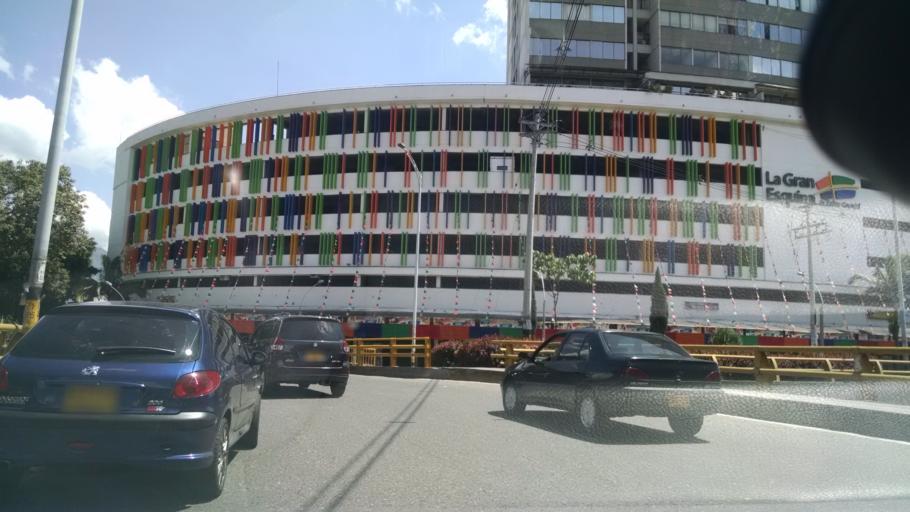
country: CO
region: Antioquia
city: Medellin
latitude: 6.2504
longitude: -75.6024
